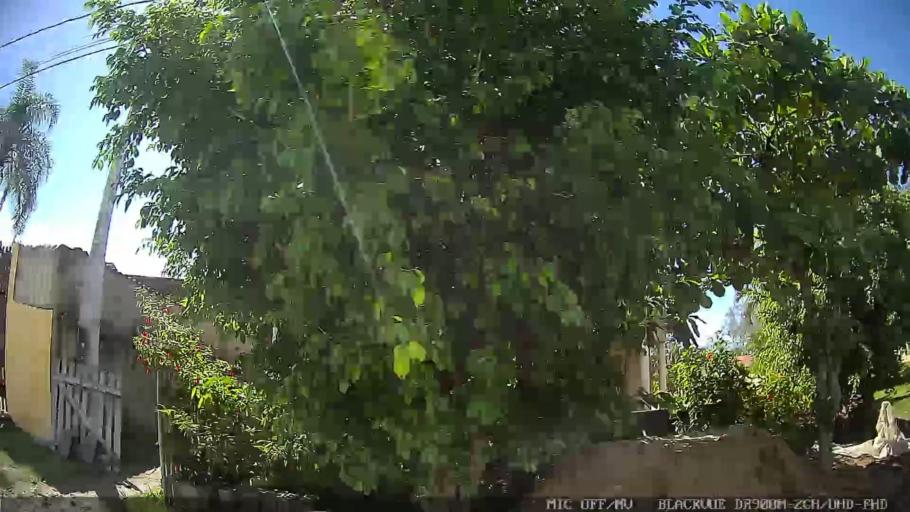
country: BR
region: Sao Paulo
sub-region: Itanhaem
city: Itanhaem
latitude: -24.2204
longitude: -46.8561
